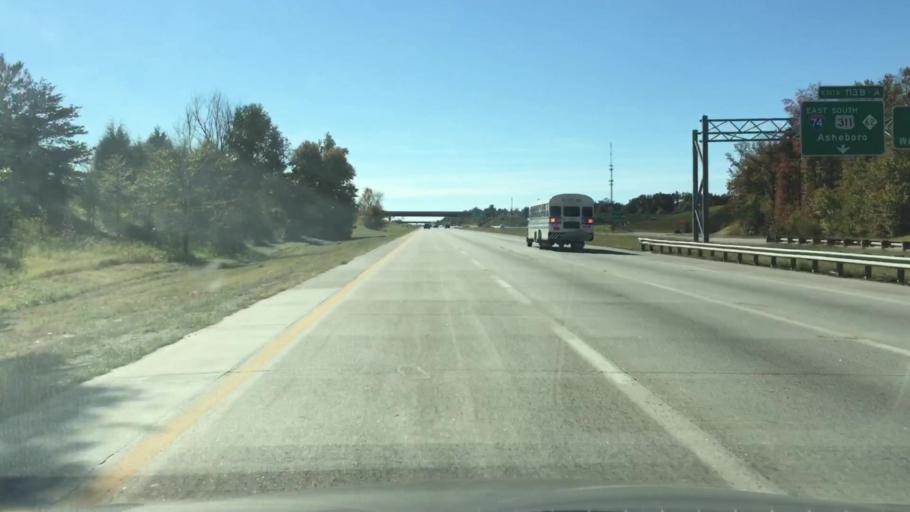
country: US
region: North Carolina
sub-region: Randolph County
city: Archdale
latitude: 35.9316
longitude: -79.9207
